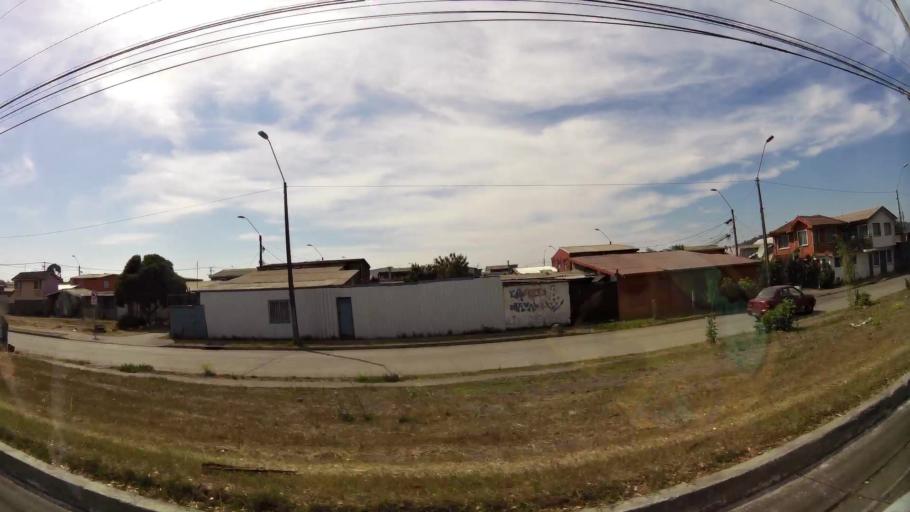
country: CL
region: Biobio
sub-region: Provincia de Concepcion
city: Talcahuano
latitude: -36.7314
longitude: -73.1183
